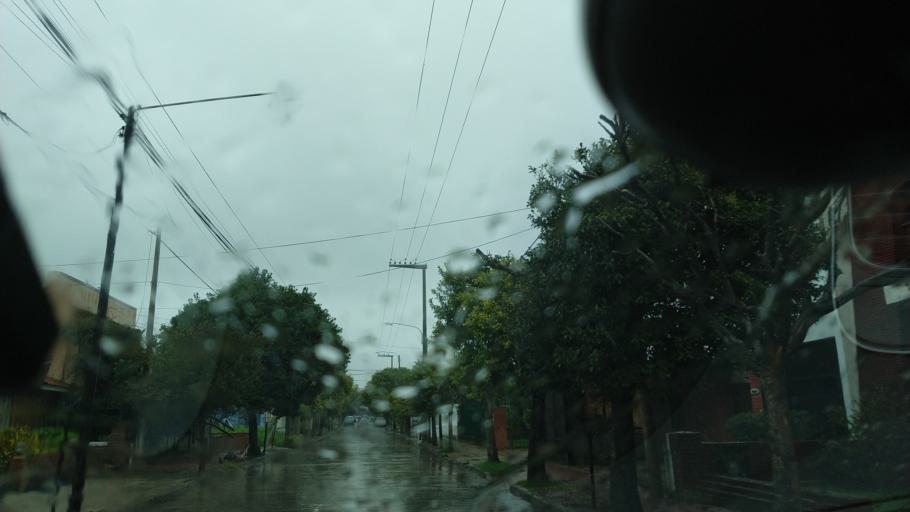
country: AR
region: Cordoba
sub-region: Departamento de Capital
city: Cordoba
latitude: -31.3664
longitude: -64.2309
